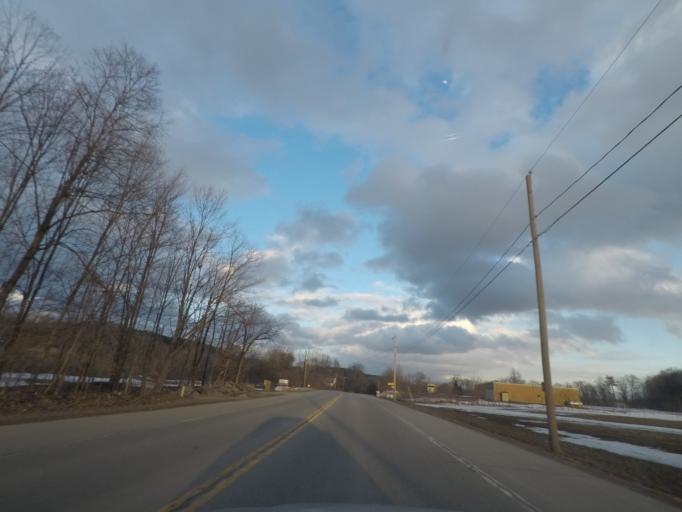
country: US
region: New York
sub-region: Montgomery County
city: Saint Johnsville
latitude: 43.0032
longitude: -74.7081
